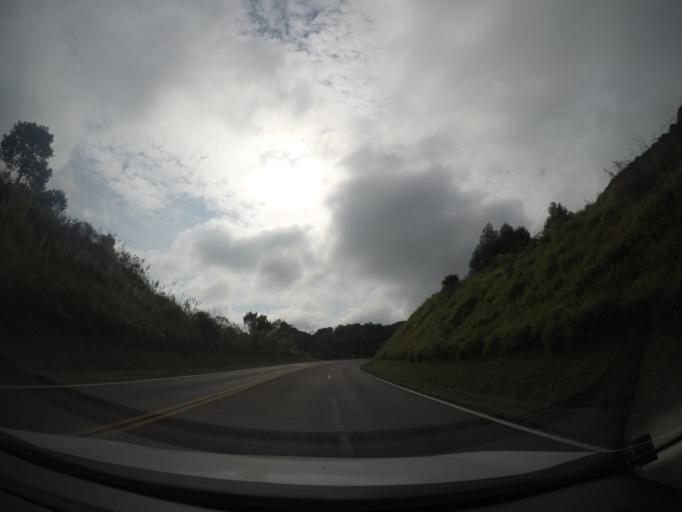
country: BR
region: Parana
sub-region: Colombo
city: Colombo
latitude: -25.3421
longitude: -49.2258
